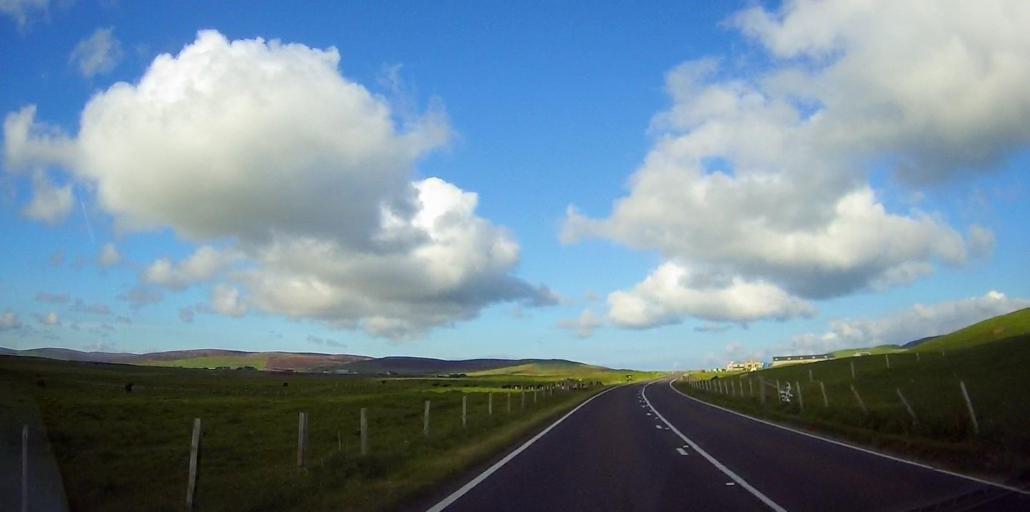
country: GB
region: Scotland
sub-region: Orkney Islands
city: Stromness
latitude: 59.0030
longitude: -3.1719
